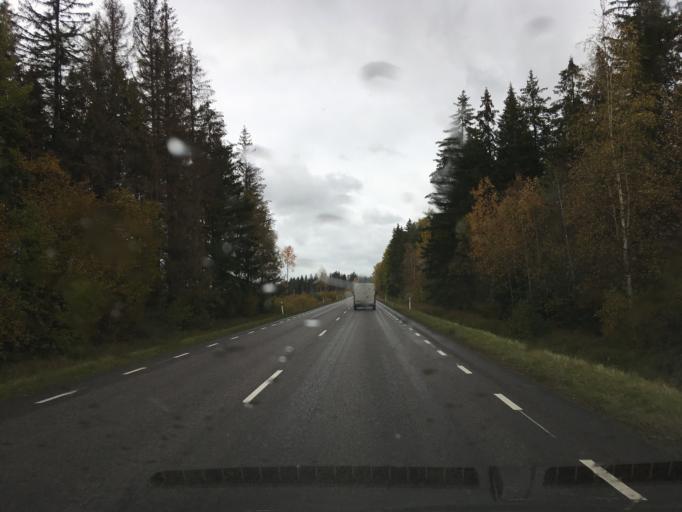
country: EE
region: Harju
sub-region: Anija vald
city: Kehra
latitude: 59.3353
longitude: 25.3119
